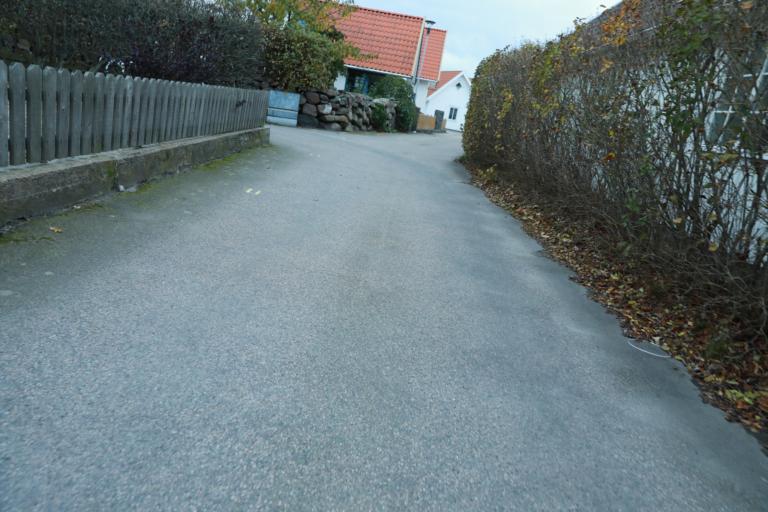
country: SE
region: Halland
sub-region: Varbergs Kommun
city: Traslovslage
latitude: 57.0575
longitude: 12.2732
